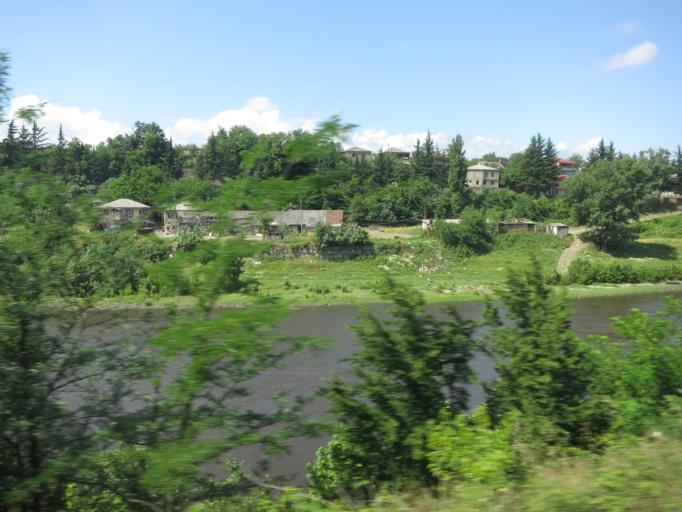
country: GE
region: Imereti
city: Zestap'oni
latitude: 42.1062
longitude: 43.0546
